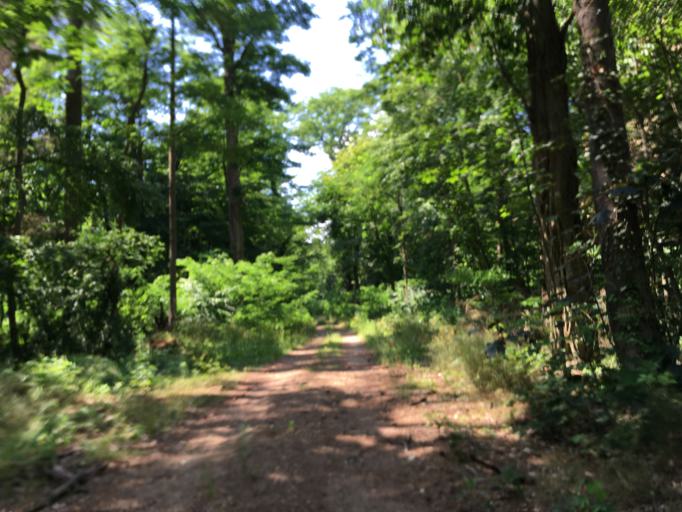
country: DE
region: Brandenburg
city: Rudnitz
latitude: 52.6714
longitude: 13.6456
